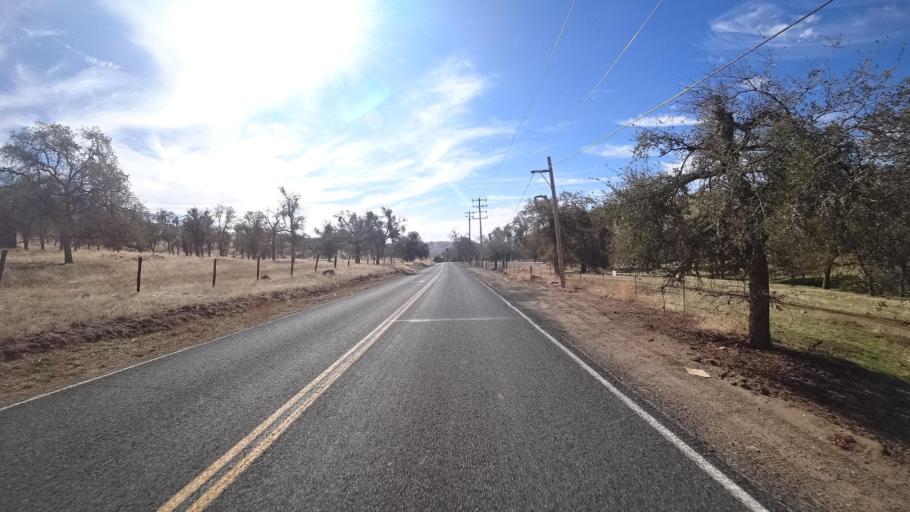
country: US
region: California
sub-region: Kern County
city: Alta Sierra
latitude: 35.6372
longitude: -118.8009
